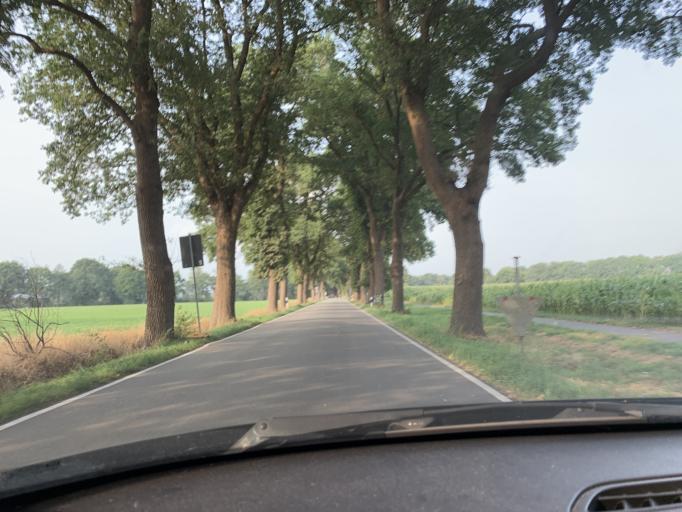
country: DE
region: Lower Saxony
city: Apen
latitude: 53.1791
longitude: 7.7796
